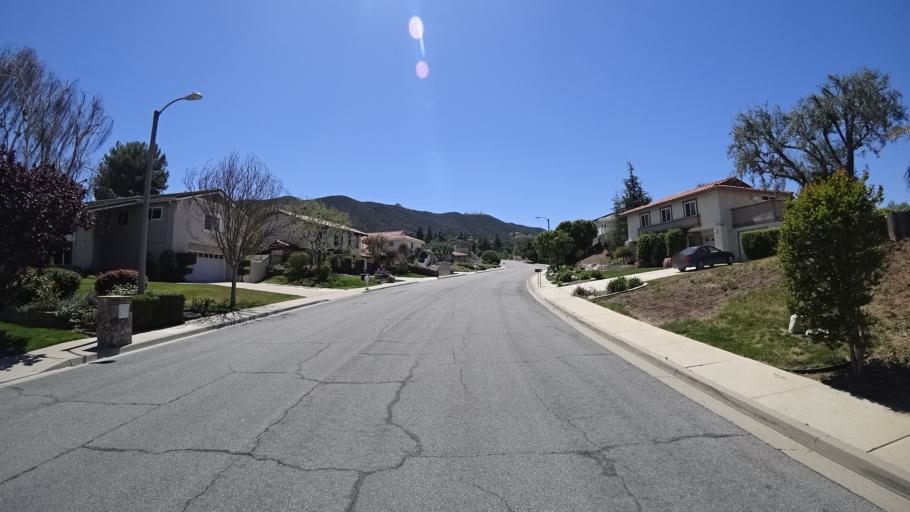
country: US
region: California
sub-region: Ventura County
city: Casa Conejo
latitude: 34.1762
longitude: -118.9010
